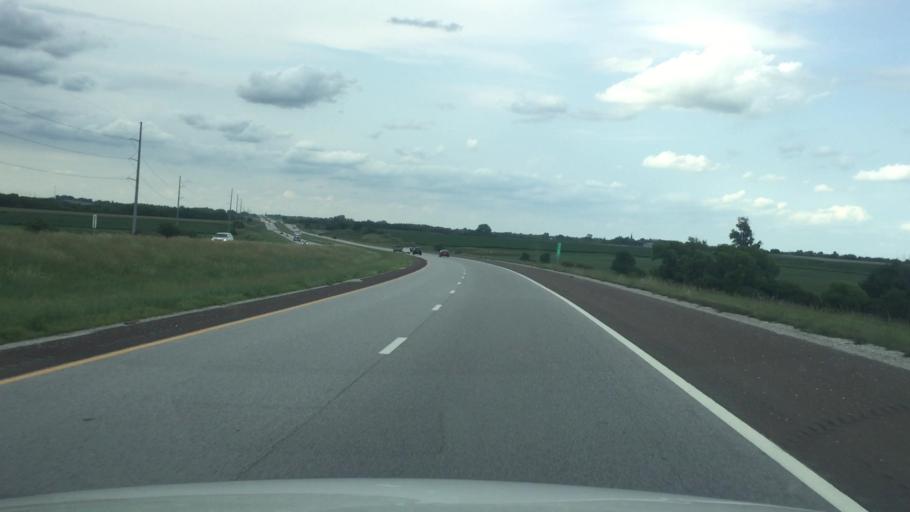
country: US
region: Kansas
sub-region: Miami County
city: Louisburg
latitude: 38.6957
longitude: -94.6767
